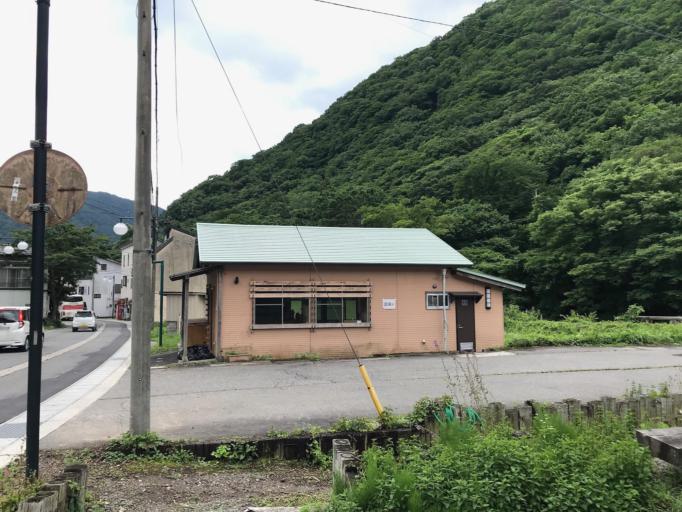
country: JP
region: Gunma
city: Numata
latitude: 36.8072
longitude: 138.9863
